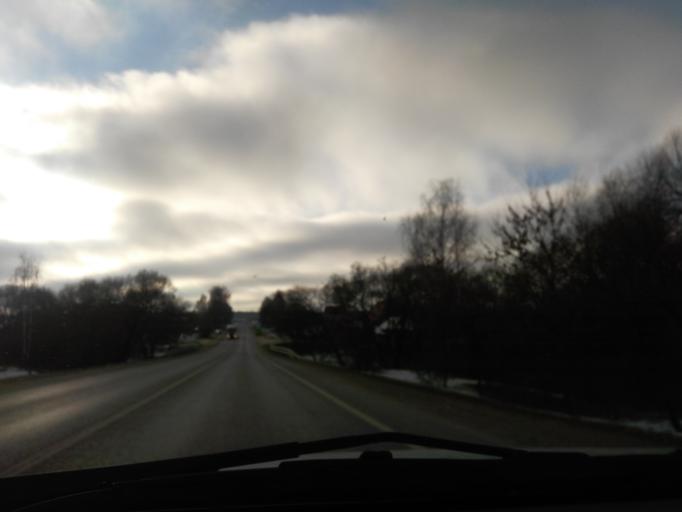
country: RU
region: Moskovskaya
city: Selyatino
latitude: 55.2813
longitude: 37.1187
